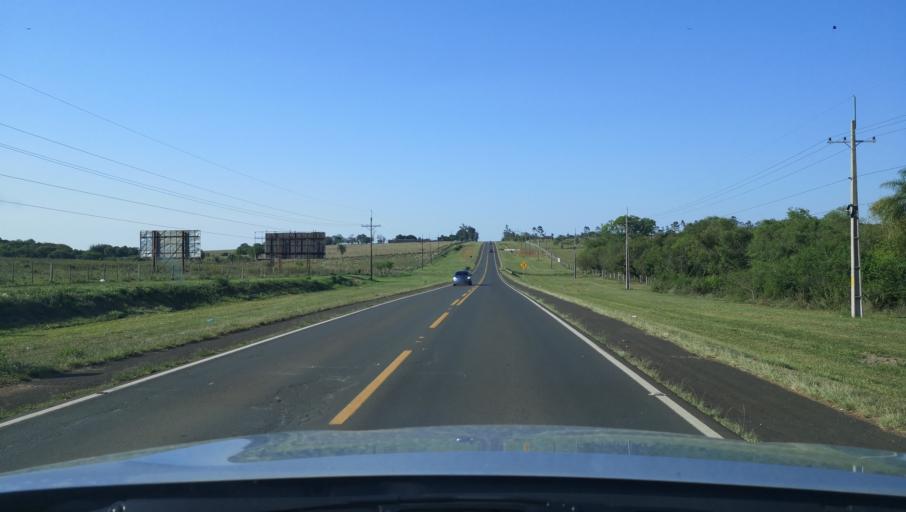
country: PY
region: Misiones
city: Santa Maria
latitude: -26.8317
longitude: -57.0317
